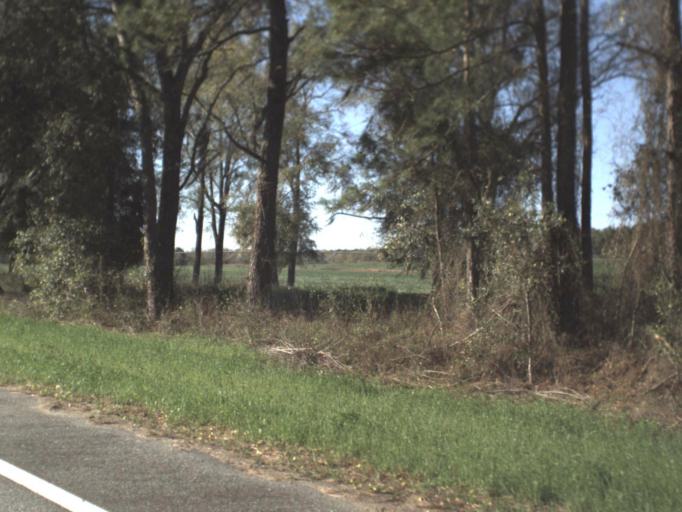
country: US
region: Georgia
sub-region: Brooks County
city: Quitman
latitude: 30.6081
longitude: -83.6462
